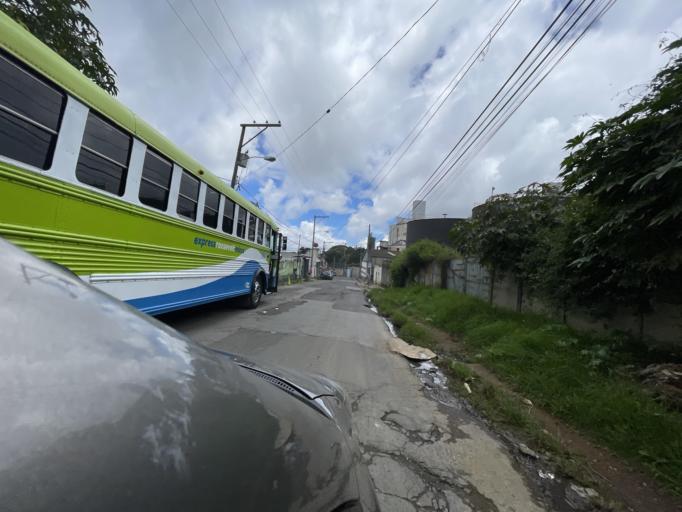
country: GT
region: Guatemala
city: Mixco
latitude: 14.6359
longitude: -90.6180
